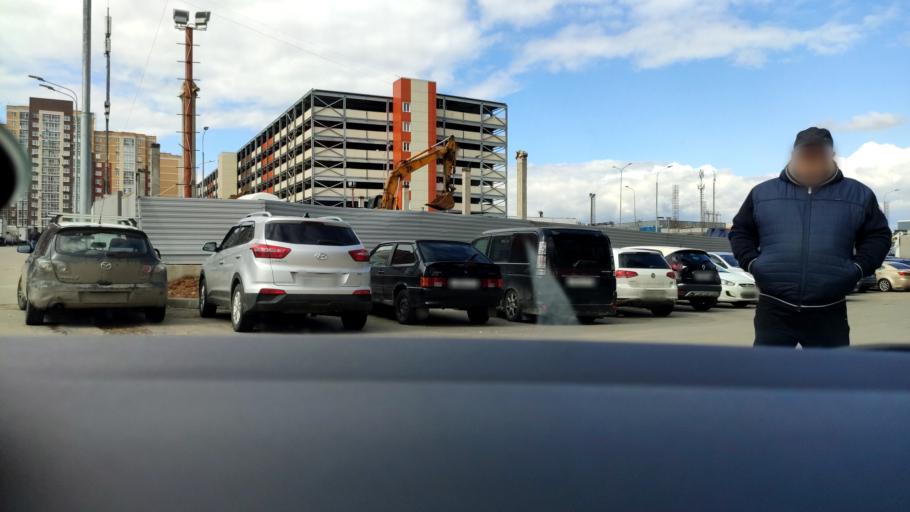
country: RU
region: Moskovskaya
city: Kommunarka
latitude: 55.5683
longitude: 37.4951
